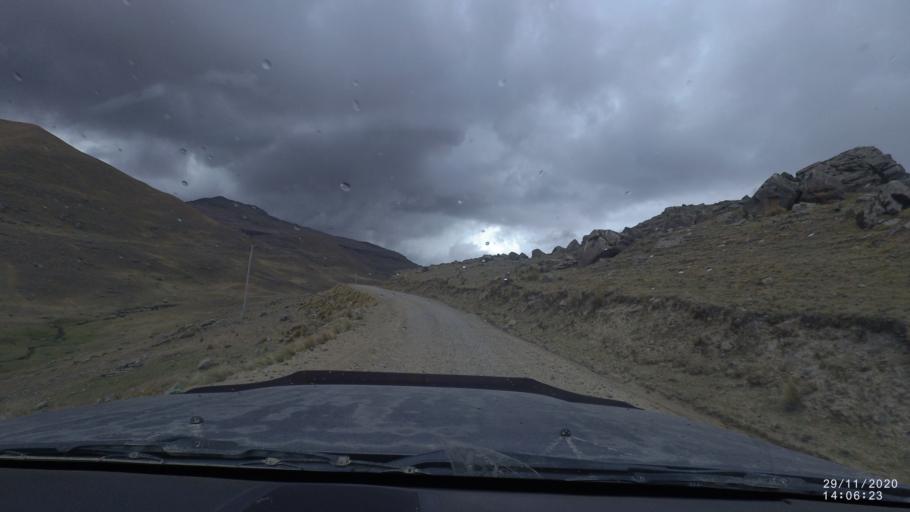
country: BO
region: Cochabamba
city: Sipe Sipe
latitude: -17.2135
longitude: -66.3783
